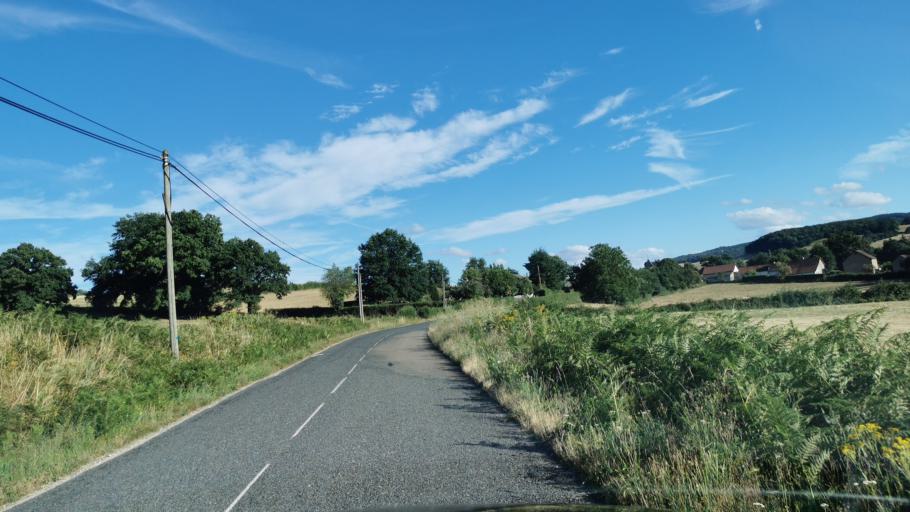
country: FR
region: Bourgogne
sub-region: Departement de Saone-et-Loire
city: Marmagne
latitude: 46.8249
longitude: 4.3223
